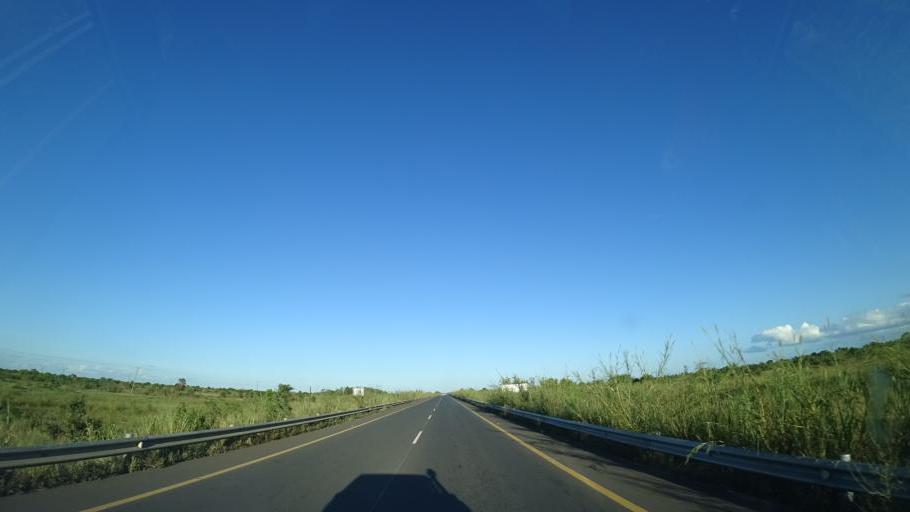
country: MZ
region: Sofala
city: Dondo
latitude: -19.3114
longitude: 34.2741
